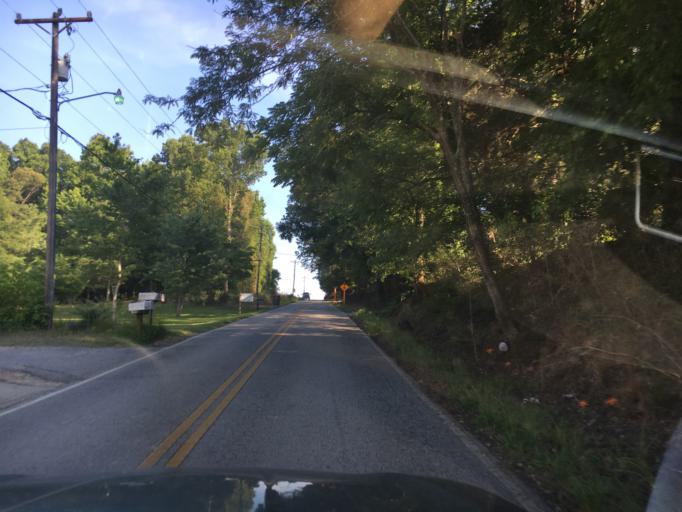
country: US
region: South Carolina
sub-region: Spartanburg County
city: Duncan
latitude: 34.8570
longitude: -82.1100
